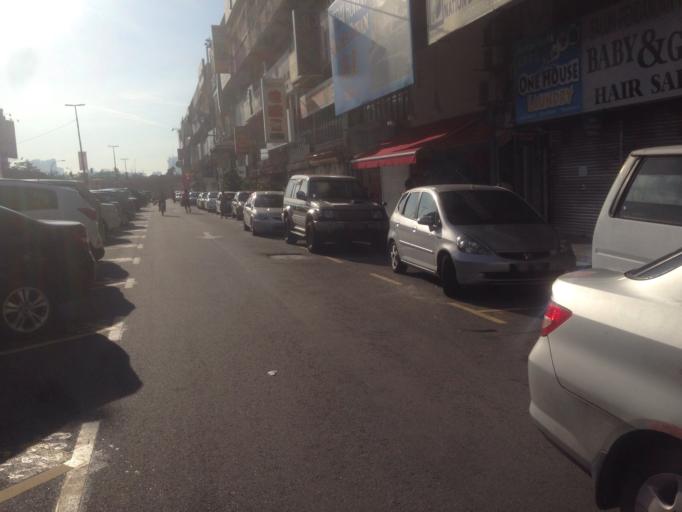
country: MY
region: Selangor
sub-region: Petaling
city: Petaling Jaya
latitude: 3.1194
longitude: 101.6223
